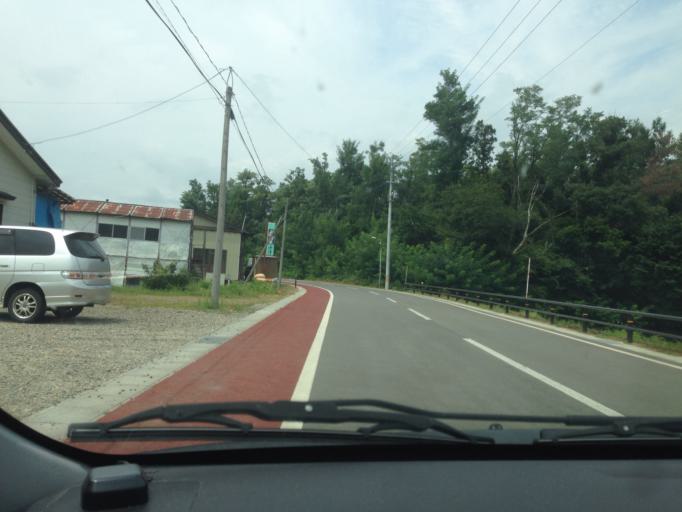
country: JP
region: Fukushima
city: Kitakata
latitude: 37.7186
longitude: 139.8776
